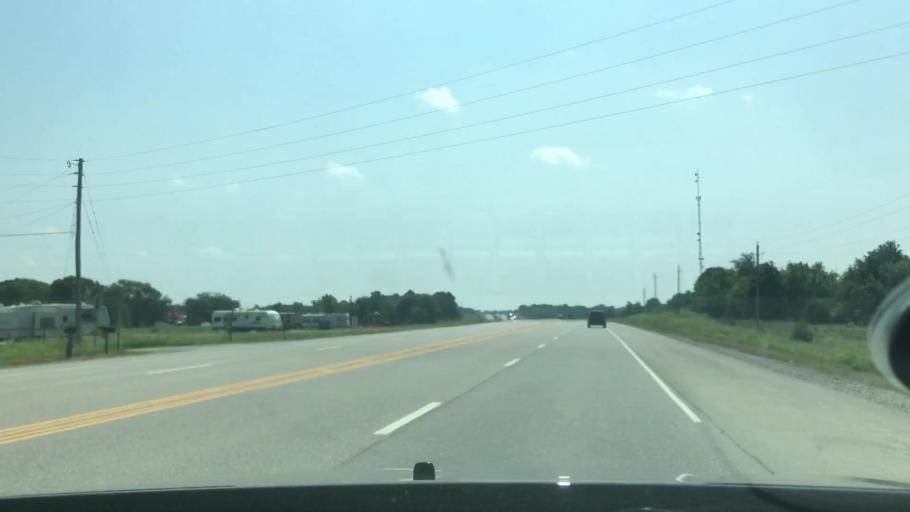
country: US
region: Oklahoma
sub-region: Atoka County
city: Atoka
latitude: 34.3602
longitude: -96.0955
